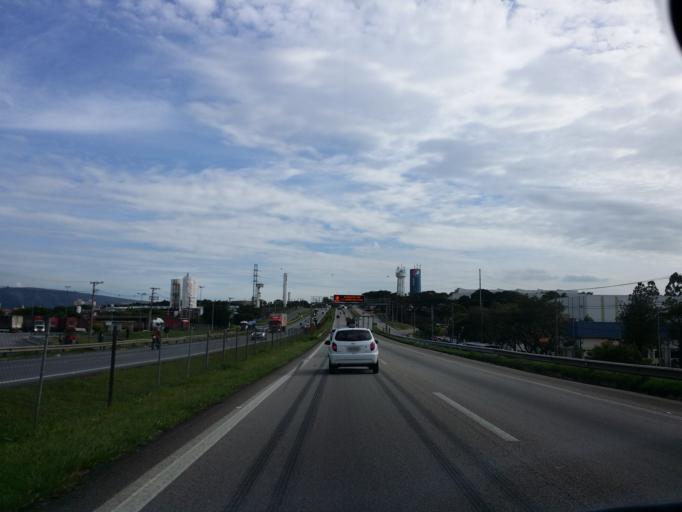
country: BR
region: Sao Paulo
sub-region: Jundiai
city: Jundiai
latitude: -23.1748
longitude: -46.9518
